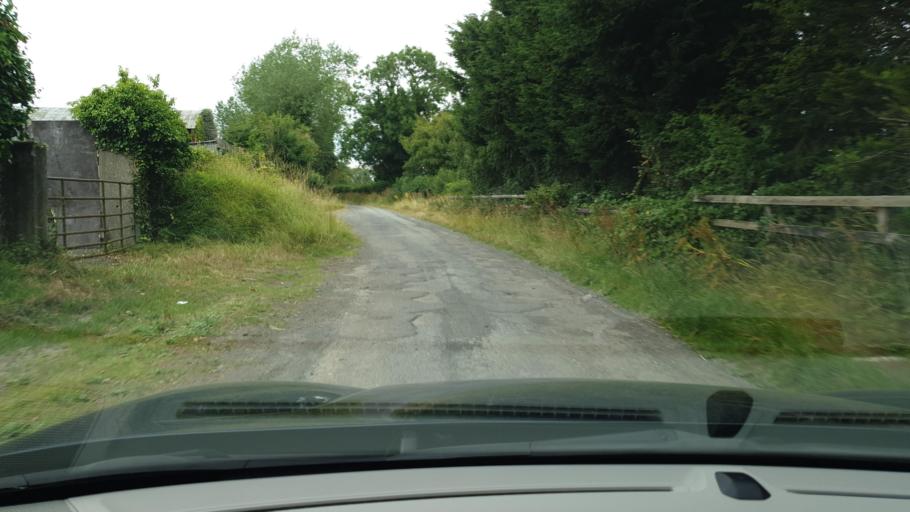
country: IE
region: Leinster
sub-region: An Mhi
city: Ashbourne
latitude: 53.5399
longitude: -6.3881
